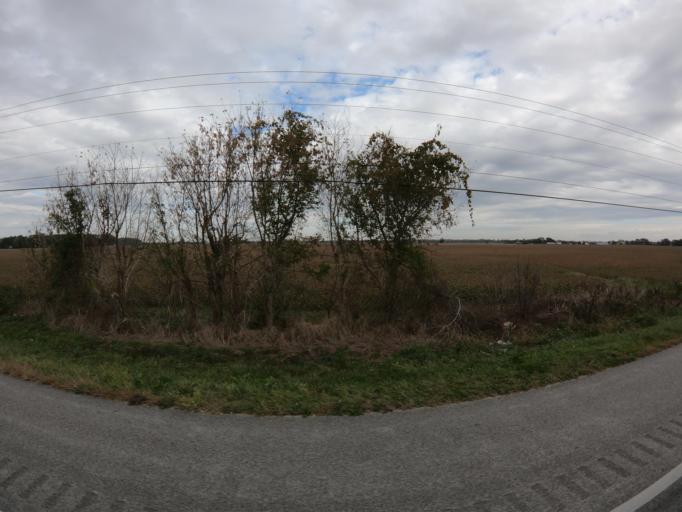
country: US
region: Maryland
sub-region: Queen Anne's County
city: Centreville
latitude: 38.9563
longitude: -76.0879
